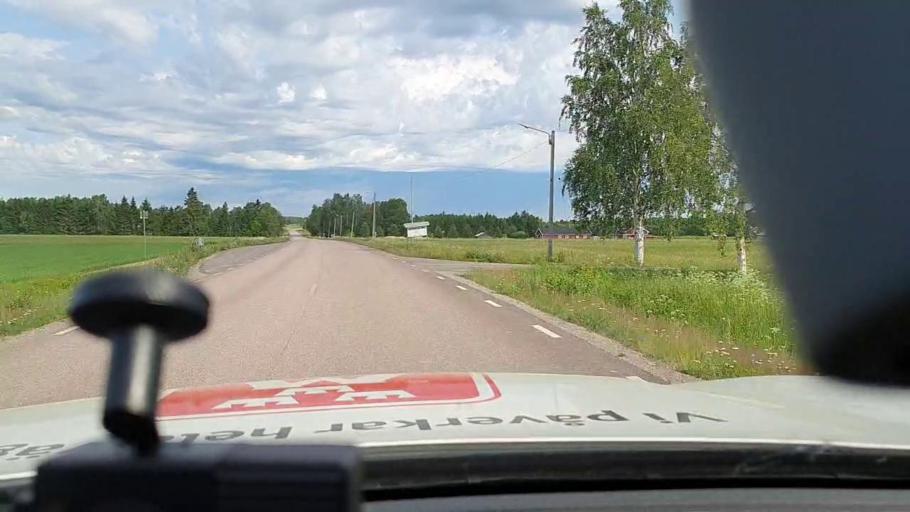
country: SE
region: Norrbotten
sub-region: Bodens Kommun
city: Saevast
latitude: 65.6944
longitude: 21.7805
